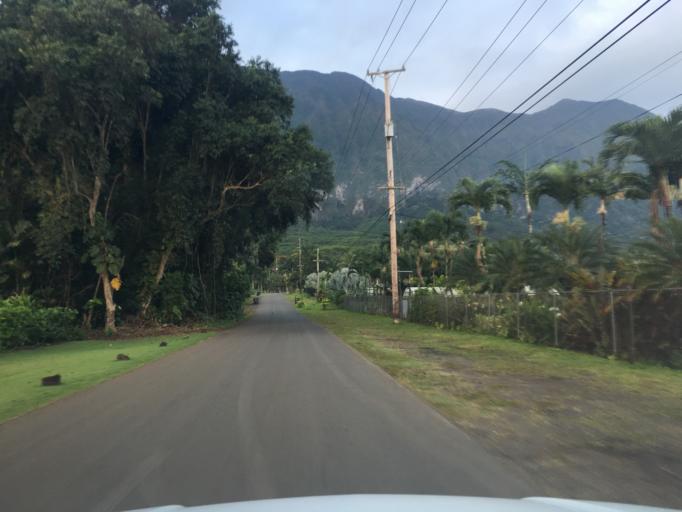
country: US
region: Hawaii
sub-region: Honolulu County
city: Waimanalo
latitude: 21.3379
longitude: -157.7380
